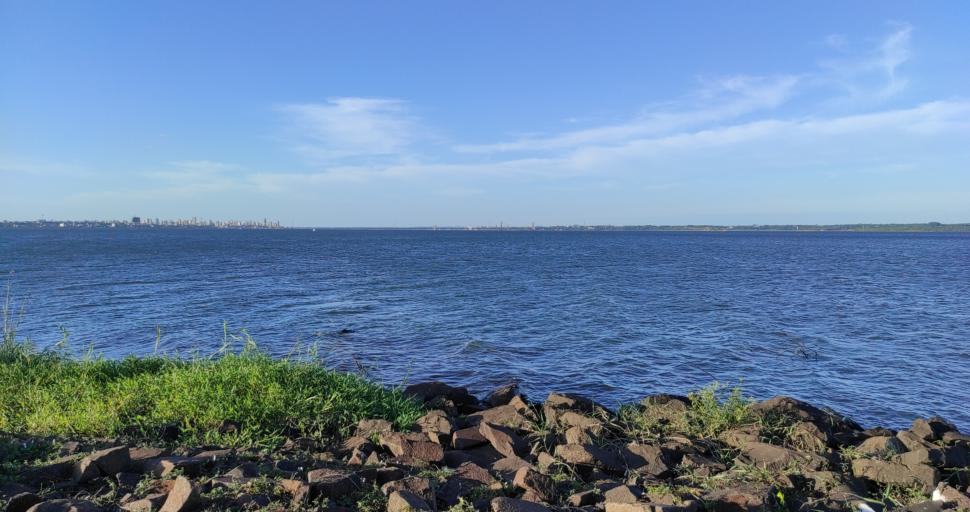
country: AR
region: Misiones
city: Garupa
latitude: -27.4304
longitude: -55.8625
